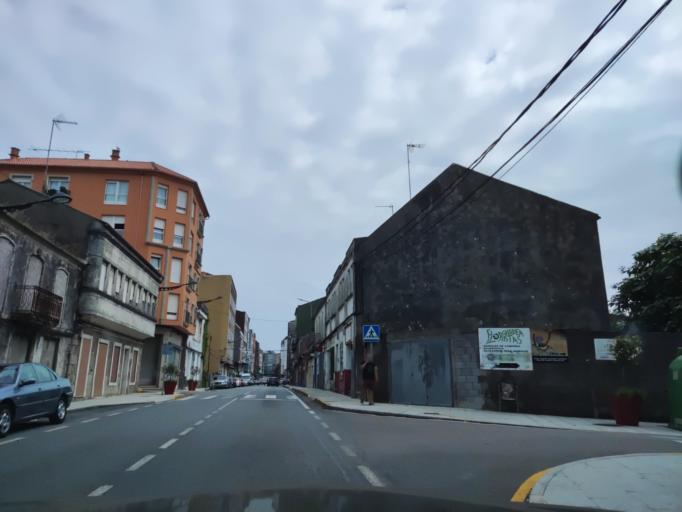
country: ES
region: Galicia
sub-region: Provincia da Coruna
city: Boiro
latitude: 42.6465
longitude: -8.8869
